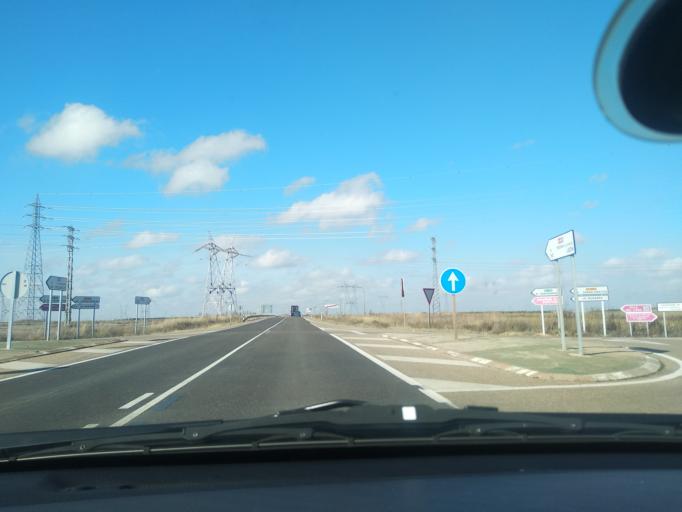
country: ES
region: Castille and Leon
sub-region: Provincia de Valladolid
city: Valdenebro de los Valles
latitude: 41.7865
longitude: -4.9430
